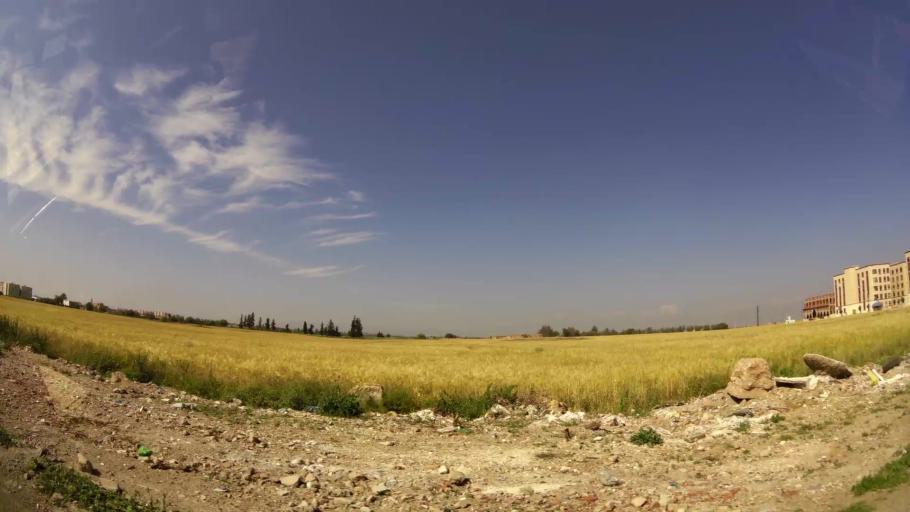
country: MA
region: Oriental
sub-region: Oujda-Angad
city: Oujda
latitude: 34.7000
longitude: -1.8779
